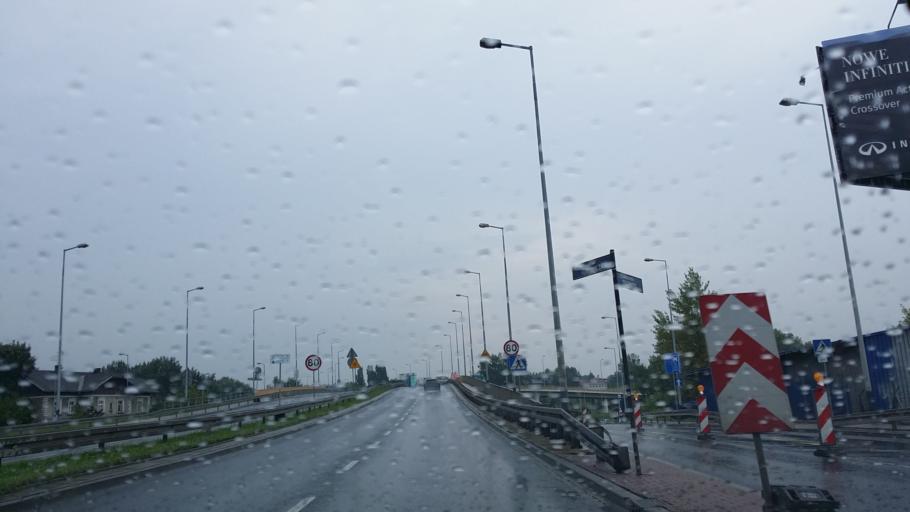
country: PL
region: Lesser Poland Voivodeship
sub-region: Krakow
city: Krakow
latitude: 50.0309
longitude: 19.9451
